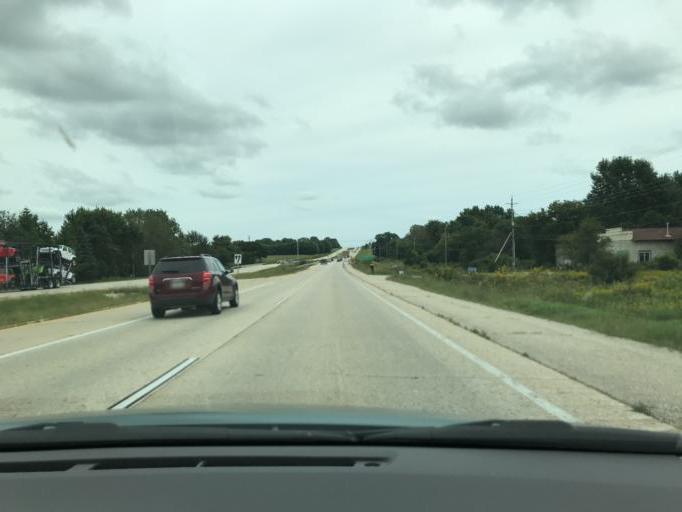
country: US
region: Wisconsin
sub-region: Kenosha County
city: Bristol
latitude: 42.5680
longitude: -88.0222
